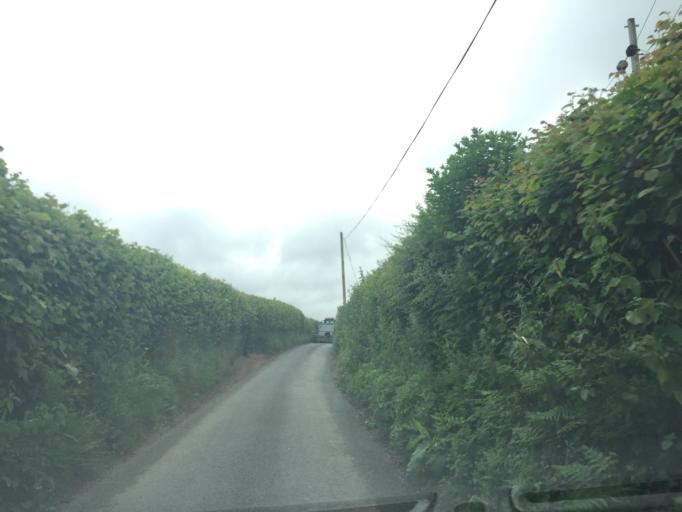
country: GB
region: England
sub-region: Dorset
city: Bovington Camp
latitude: 50.7275
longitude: -2.3297
